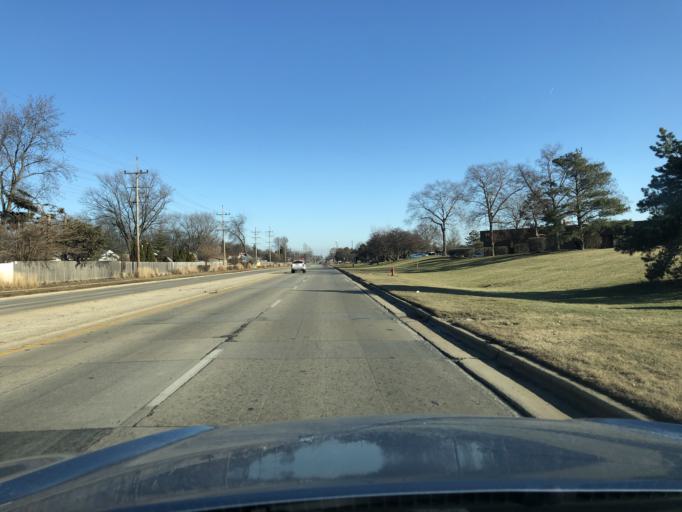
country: US
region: Illinois
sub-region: DuPage County
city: Itasca
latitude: 41.9925
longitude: -88.0121
